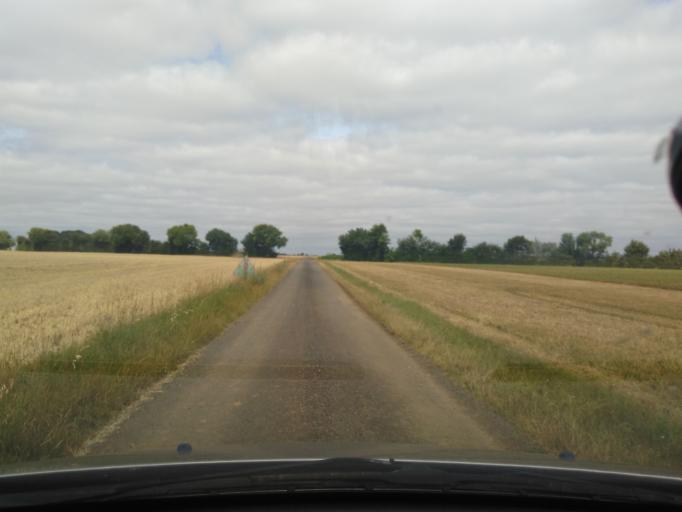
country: FR
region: Pays de la Loire
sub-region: Departement de la Vendee
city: Sainte-Gemme-la-Plaine
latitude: 46.5244
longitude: -1.0952
